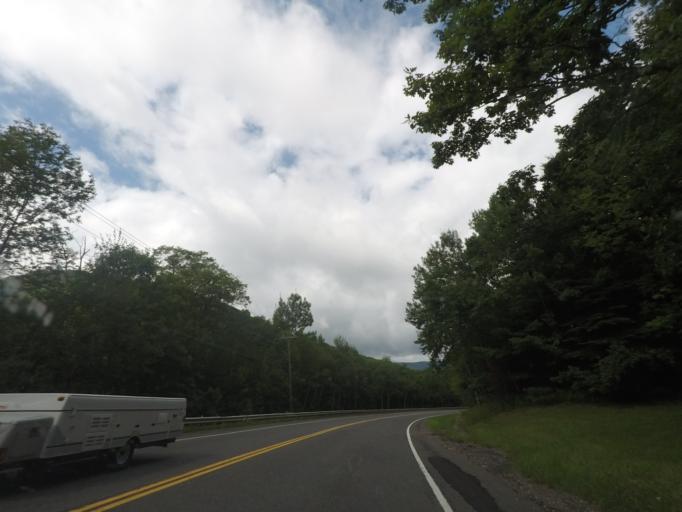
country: US
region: Massachusetts
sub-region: Berkshire County
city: Lanesborough
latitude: 42.5643
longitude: -73.2680
